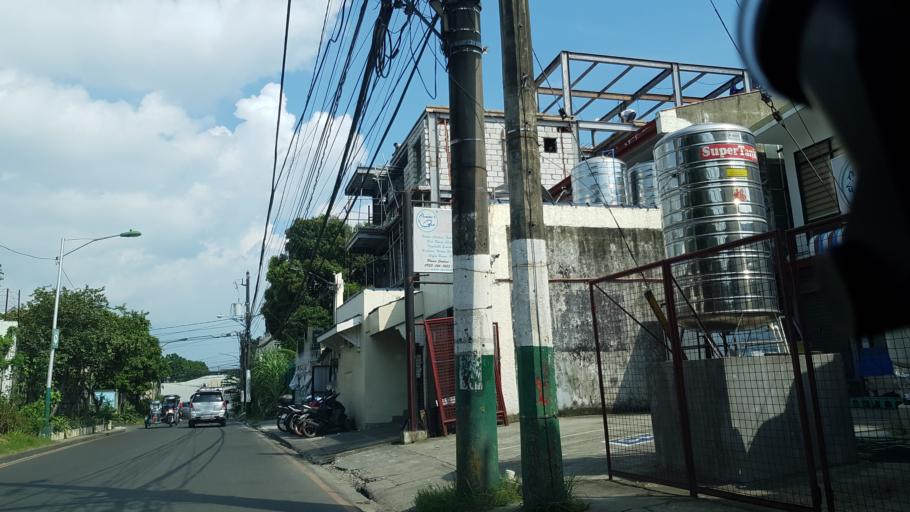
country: PH
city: Sambayanihan People's Village
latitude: 14.4782
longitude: 121.0297
